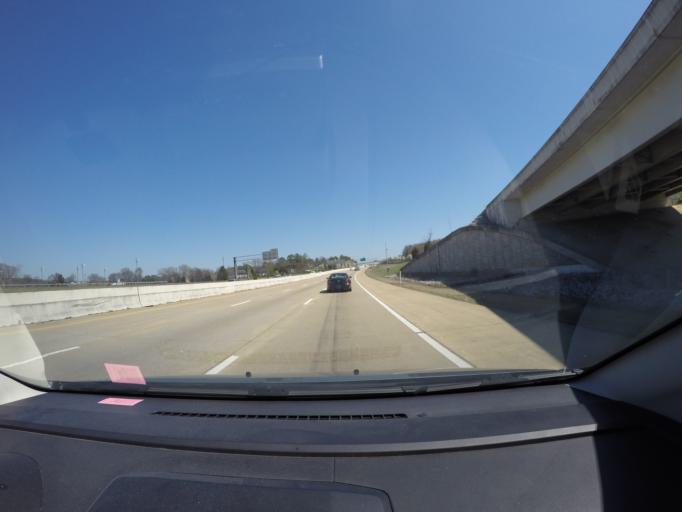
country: US
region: Tennessee
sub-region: Hamilton County
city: East Brainerd
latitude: 35.0282
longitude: -85.1715
